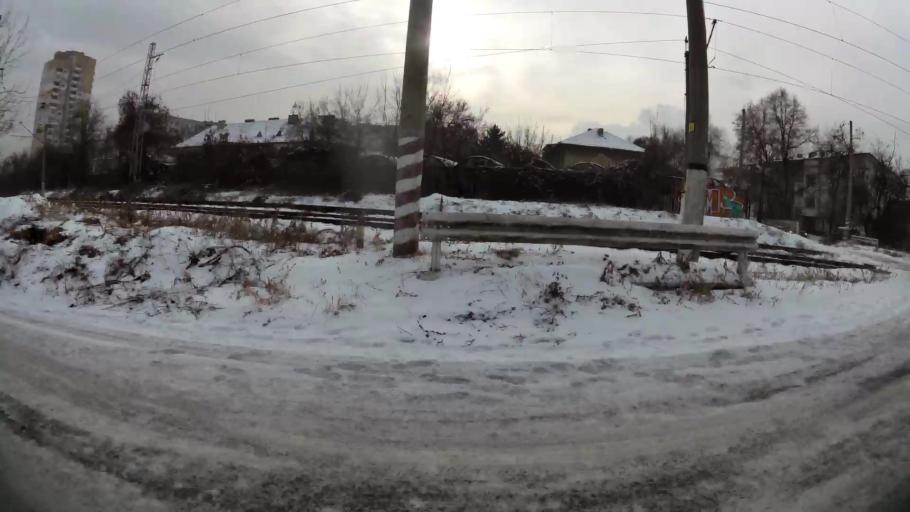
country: BG
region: Sofia-Capital
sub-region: Stolichna Obshtina
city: Sofia
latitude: 42.7164
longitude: 23.3020
